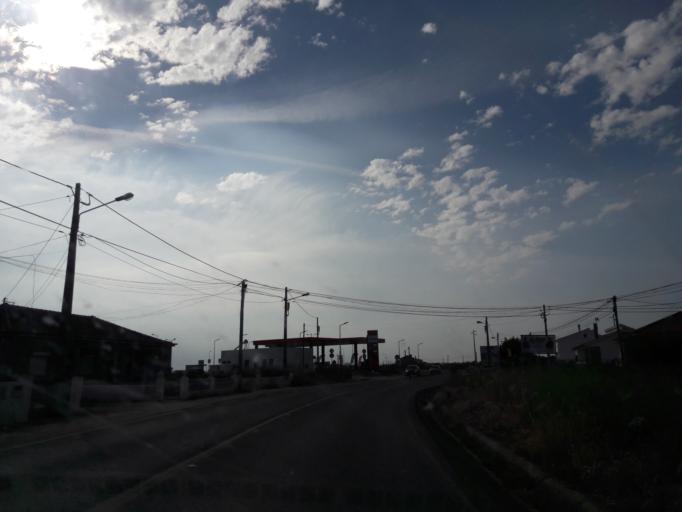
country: PT
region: Leiria
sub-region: Peniche
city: Atouguia da Baleia
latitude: 39.3448
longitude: -9.3391
